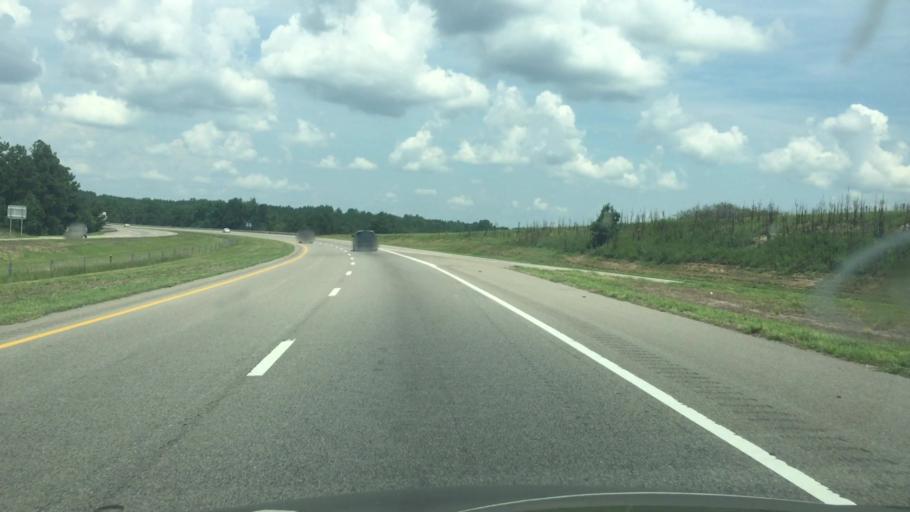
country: US
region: North Carolina
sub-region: Richmond County
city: Ellerbe
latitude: 35.1761
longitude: -79.7128
